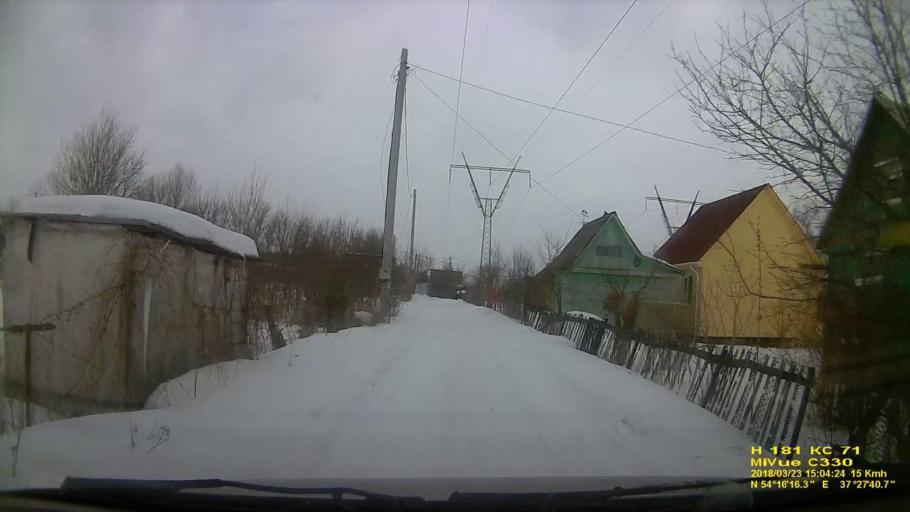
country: RU
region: Tula
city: Leninskiy
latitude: 54.2713
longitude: 37.4613
